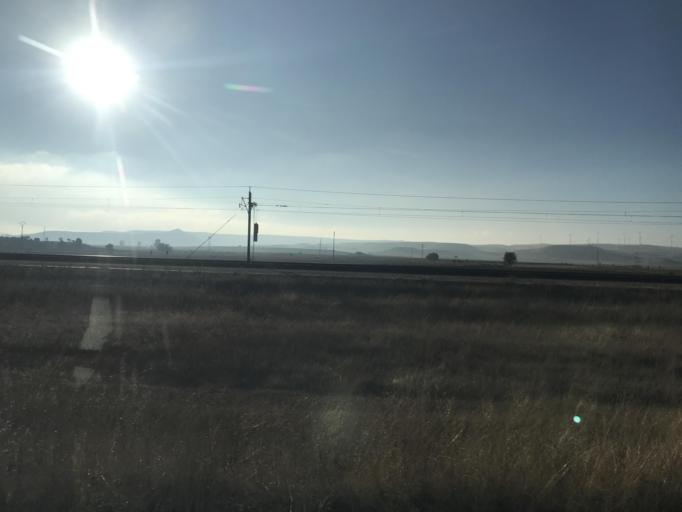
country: ES
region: Castille and Leon
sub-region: Provincia de Palencia
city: Quintana del Puente
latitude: 42.0763
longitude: -4.2043
